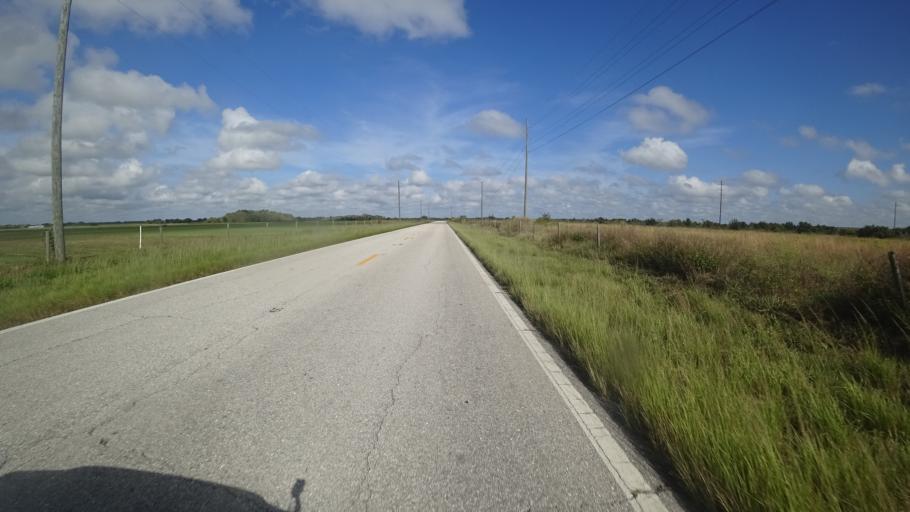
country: US
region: Florida
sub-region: Hardee County
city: Wauchula
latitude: 27.5308
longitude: -82.0771
